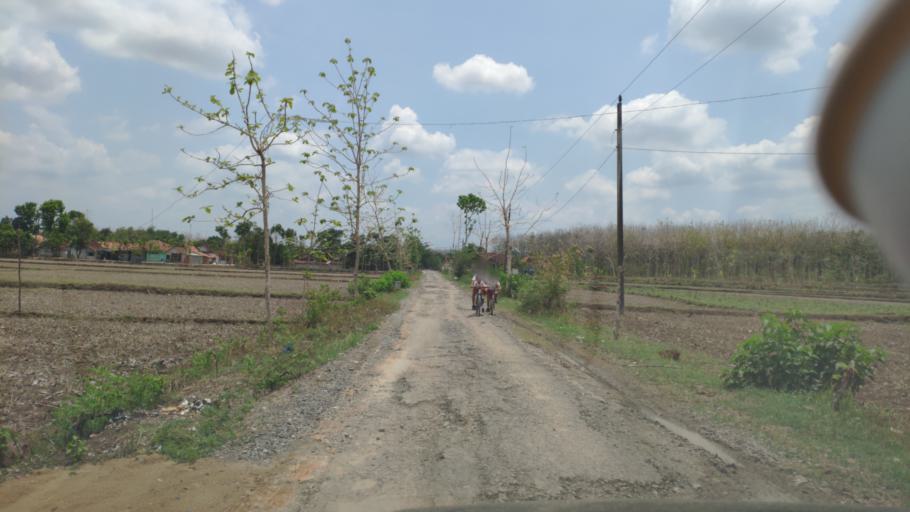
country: ID
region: Central Java
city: Gumiring
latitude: -7.0376
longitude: 111.3849
